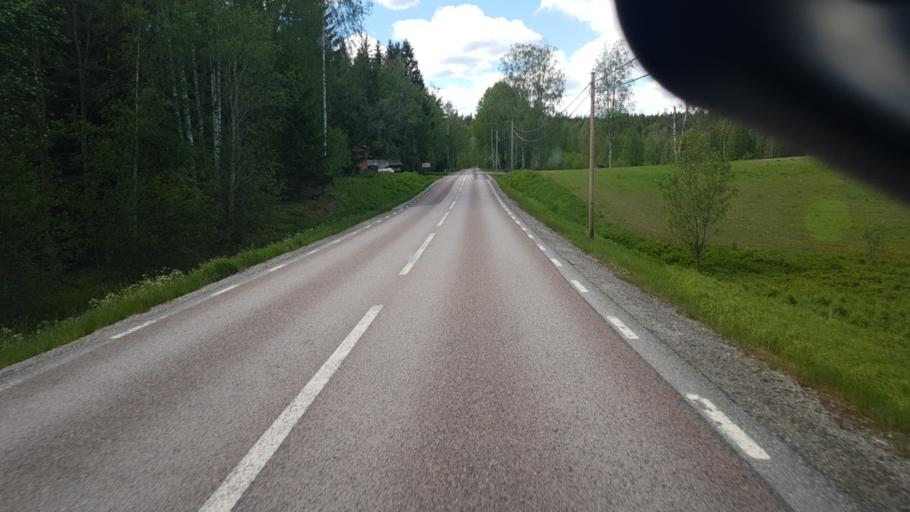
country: SE
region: Vaermland
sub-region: Sunne Kommun
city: Sunne
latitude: 59.6677
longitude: 12.9954
